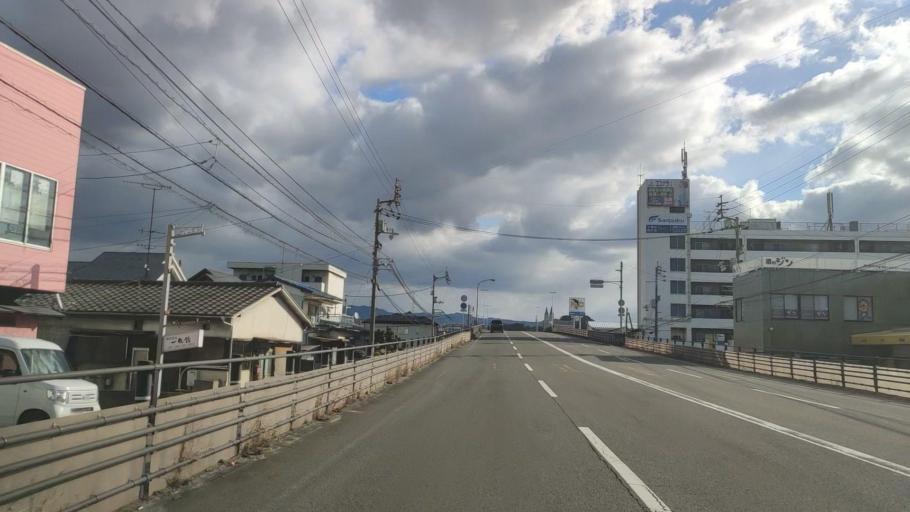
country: JP
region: Ehime
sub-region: Shikoku-chuo Shi
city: Matsuyama
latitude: 33.8573
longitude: 132.7212
